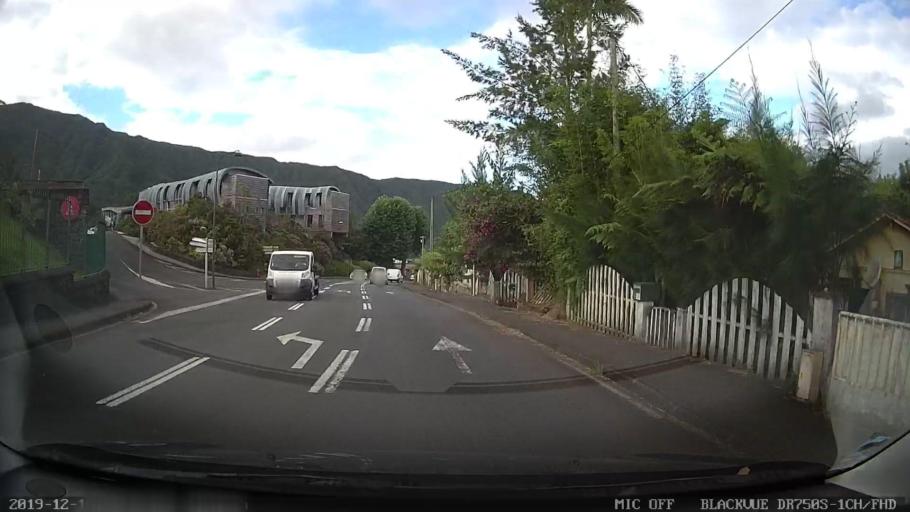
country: RE
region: Reunion
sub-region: Reunion
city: Saint-Benoit
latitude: -21.1374
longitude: 55.6245
